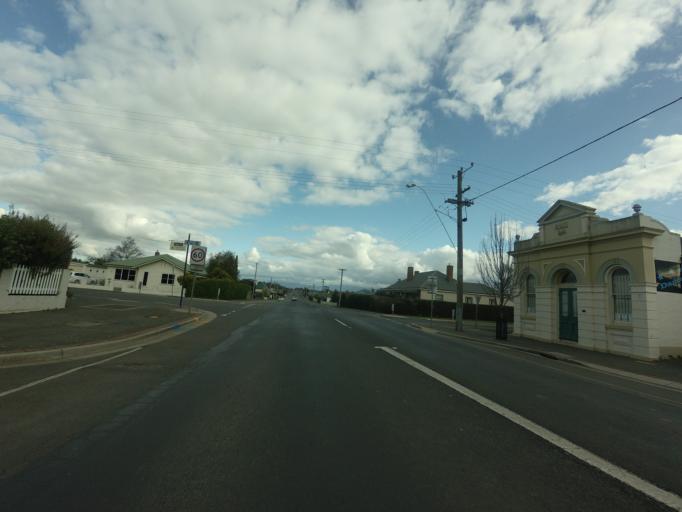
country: AU
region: Tasmania
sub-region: Northern Midlands
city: Longford
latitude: -41.5979
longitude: 147.1211
